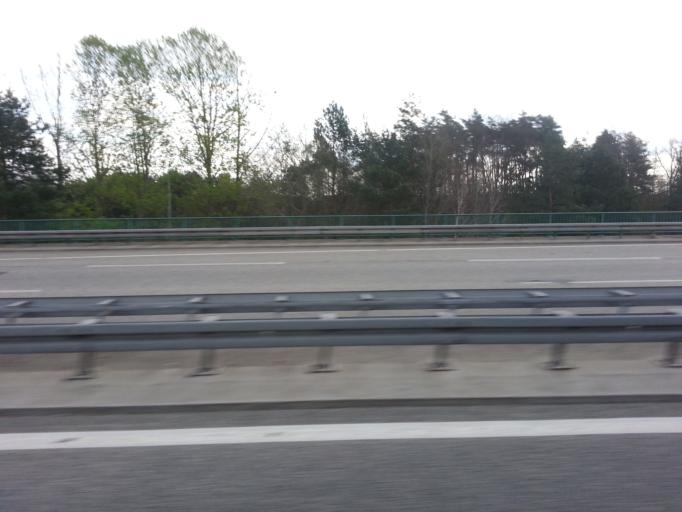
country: DE
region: Mecklenburg-Vorpommern
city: Malchow
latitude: 53.4952
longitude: 12.3824
